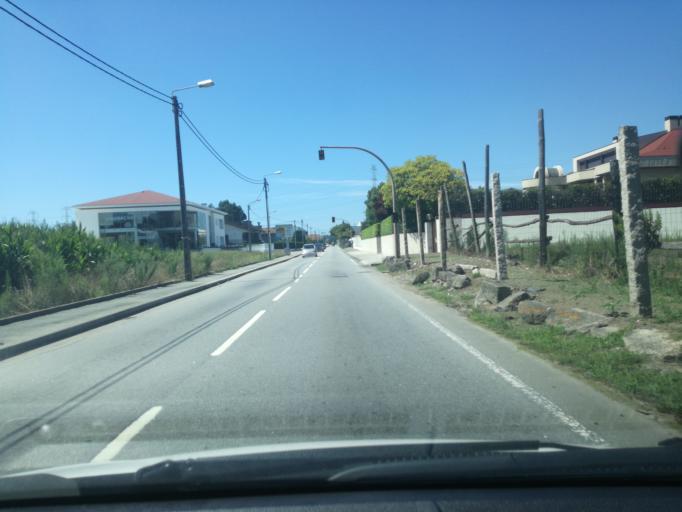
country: PT
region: Porto
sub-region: Maia
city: Nogueira
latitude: 41.2311
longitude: -8.5901
